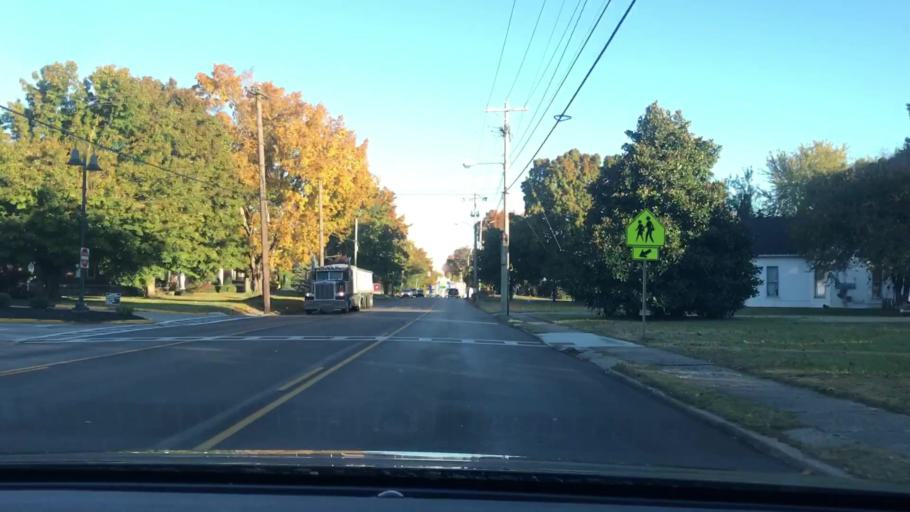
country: US
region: Kentucky
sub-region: Simpson County
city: Franklin
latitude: 36.7161
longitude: -86.5776
